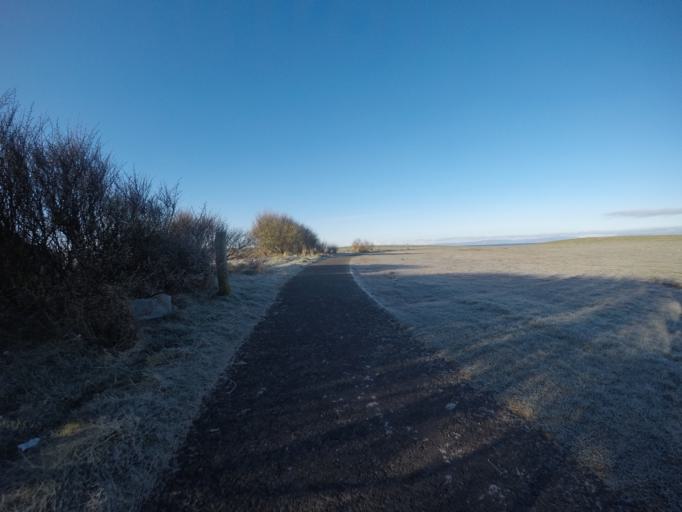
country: GB
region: Scotland
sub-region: North Ayrshire
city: Stevenston
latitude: 55.6263
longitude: -4.7457
